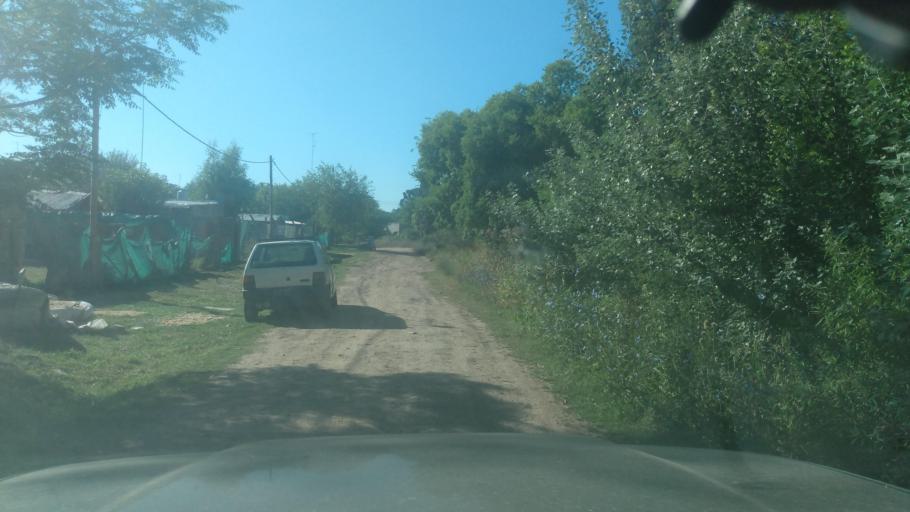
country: AR
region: Buenos Aires
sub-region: Partido de Lujan
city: Lujan
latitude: -34.5879
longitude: -59.0614
